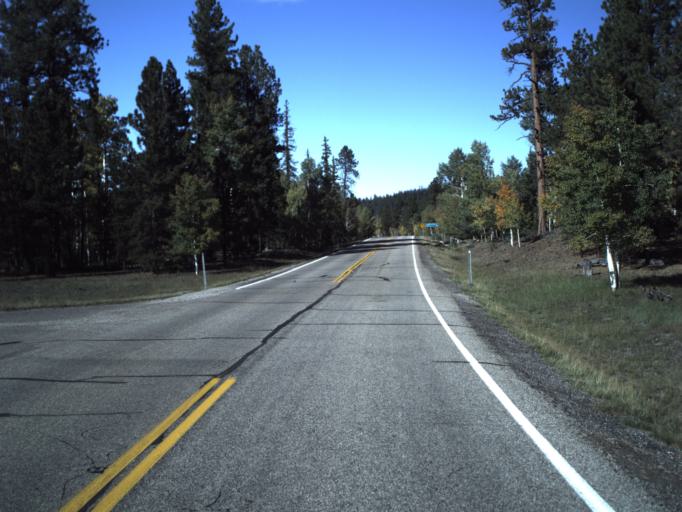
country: US
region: Utah
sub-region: Iron County
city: Parowan
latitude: 37.6689
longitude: -112.6688
